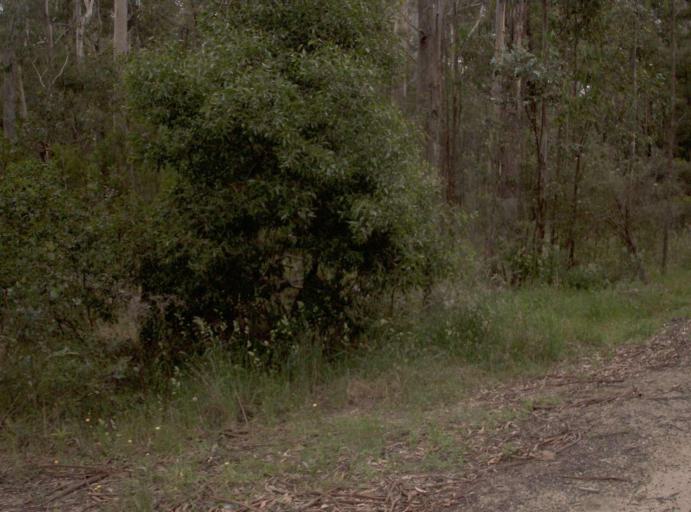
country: AU
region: New South Wales
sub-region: Bombala
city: Bombala
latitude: -37.5002
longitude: 149.1808
